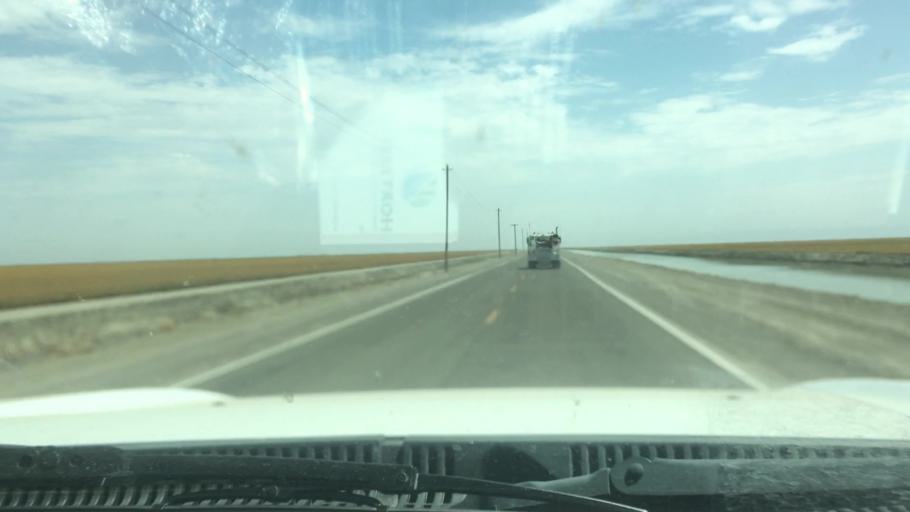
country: US
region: California
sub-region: Tulare County
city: Alpaugh
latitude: 35.9263
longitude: -119.5732
